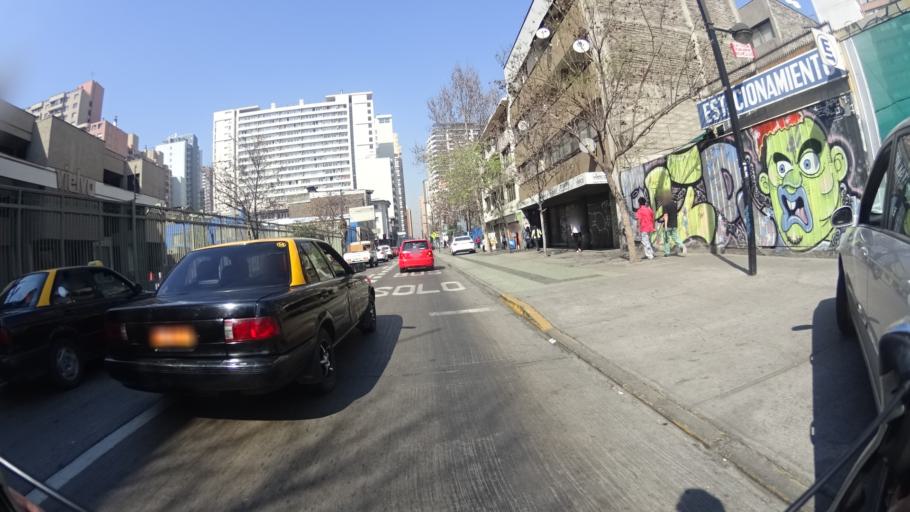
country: CL
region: Santiago Metropolitan
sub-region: Provincia de Santiago
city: Santiago
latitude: -33.4459
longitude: -70.6470
